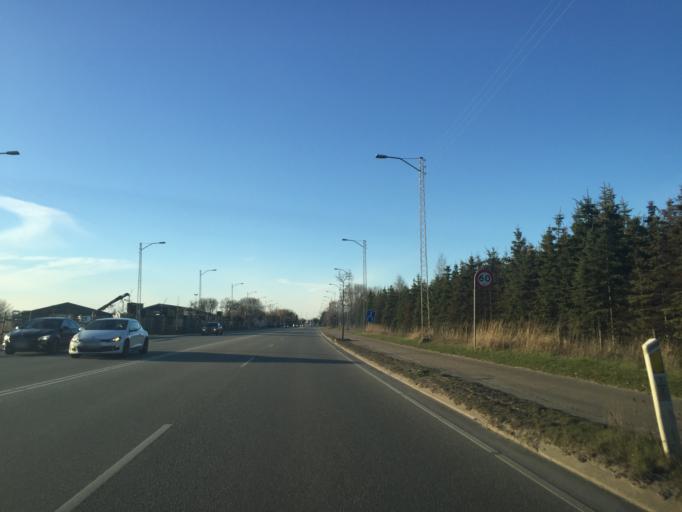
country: DK
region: Capital Region
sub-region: Tarnby Kommune
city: Tarnby
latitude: 55.6062
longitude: 12.6173
